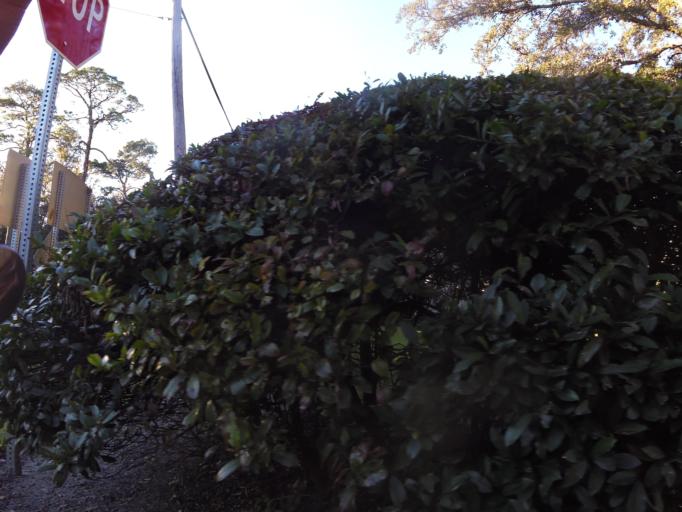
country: US
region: Florida
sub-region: Duval County
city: Jacksonville
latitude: 30.2769
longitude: -81.6991
